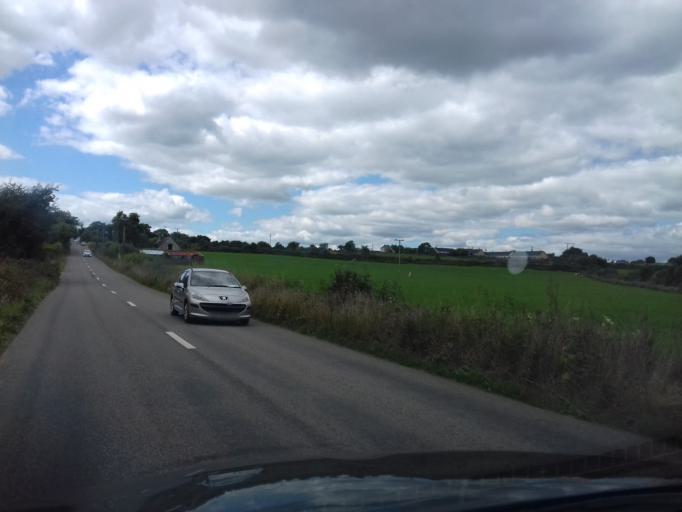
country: IE
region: Munster
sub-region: Waterford
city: Portlaw
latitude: 52.1777
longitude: -7.3264
